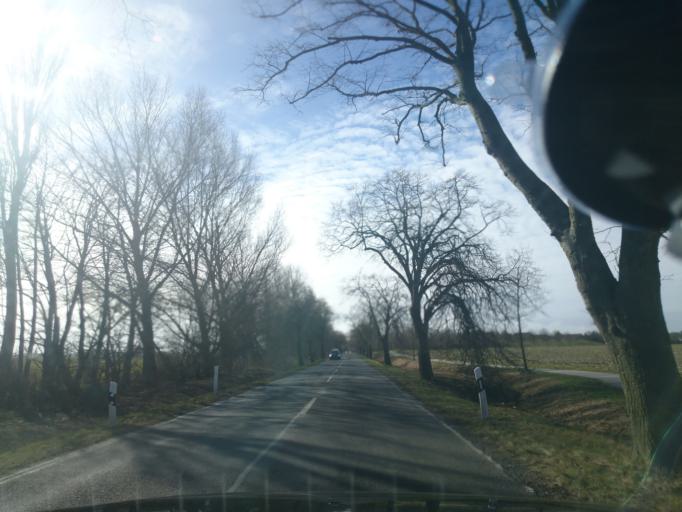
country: DE
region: Mecklenburg-Vorpommern
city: Elmenhorst
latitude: 54.1606
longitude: 12.0303
